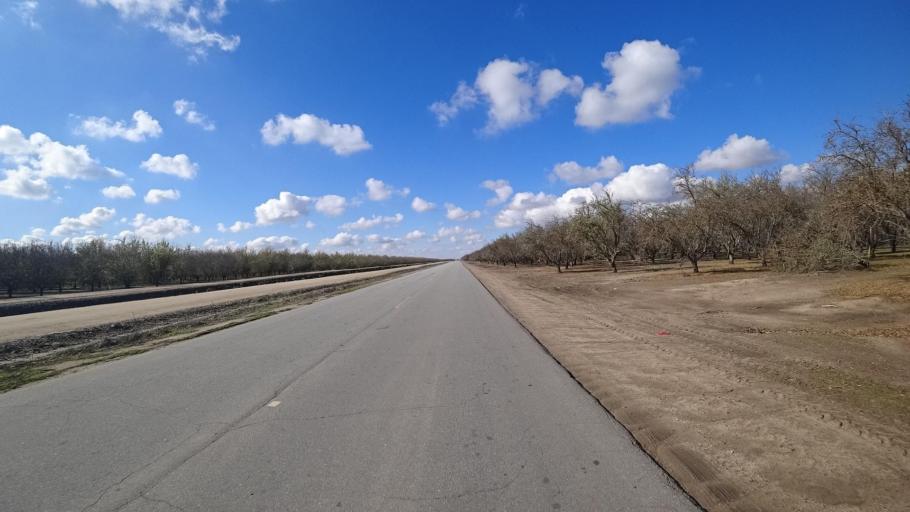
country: US
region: California
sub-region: Kern County
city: McFarland
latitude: 35.6742
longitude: -119.3041
